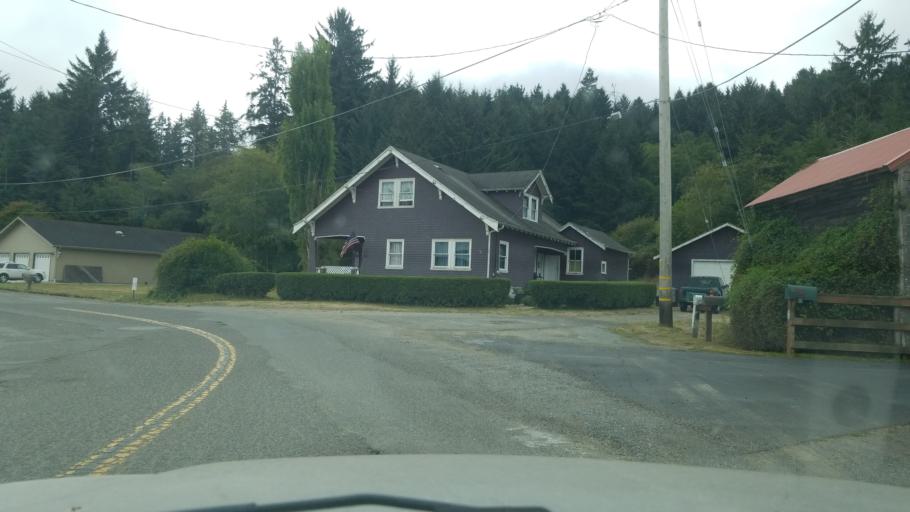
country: US
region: California
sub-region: Humboldt County
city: Ferndale
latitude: 40.5779
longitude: -124.2695
